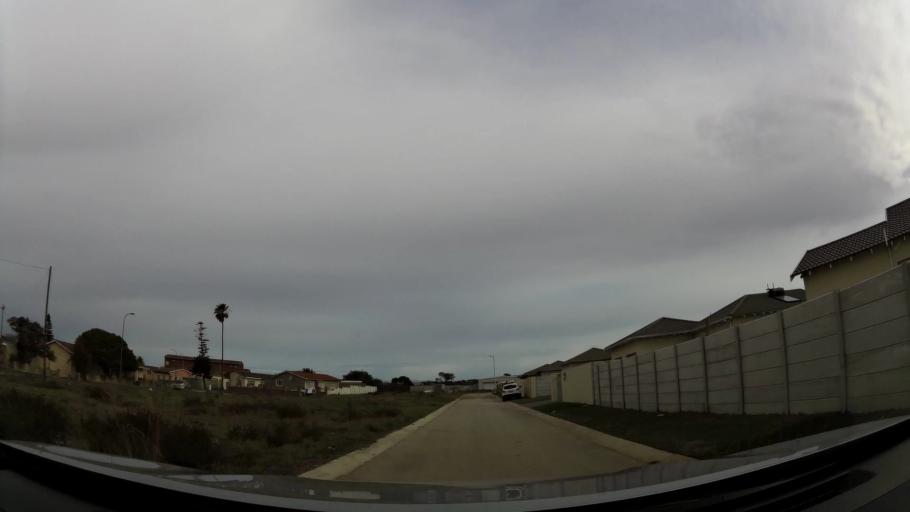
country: ZA
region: Eastern Cape
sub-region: Nelson Mandela Bay Metropolitan Municipality
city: Port Elizabeth
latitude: -33.9327
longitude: 25.5044
